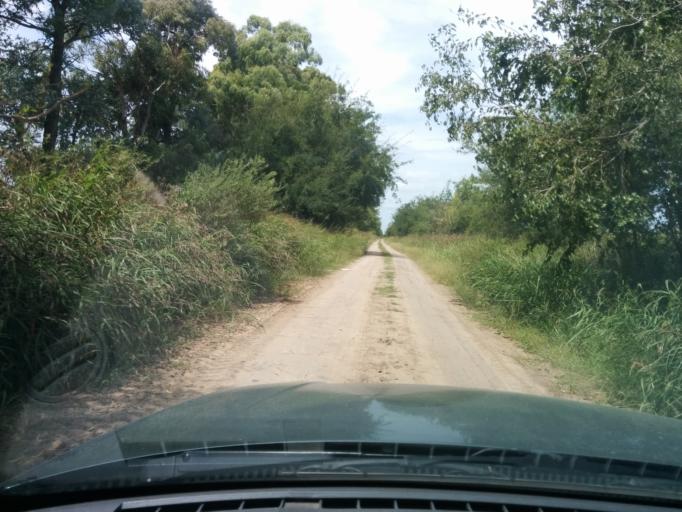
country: AR
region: Buenos Aires
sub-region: Partido de Campana
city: Campana
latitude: -34.2666
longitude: -58.9660
